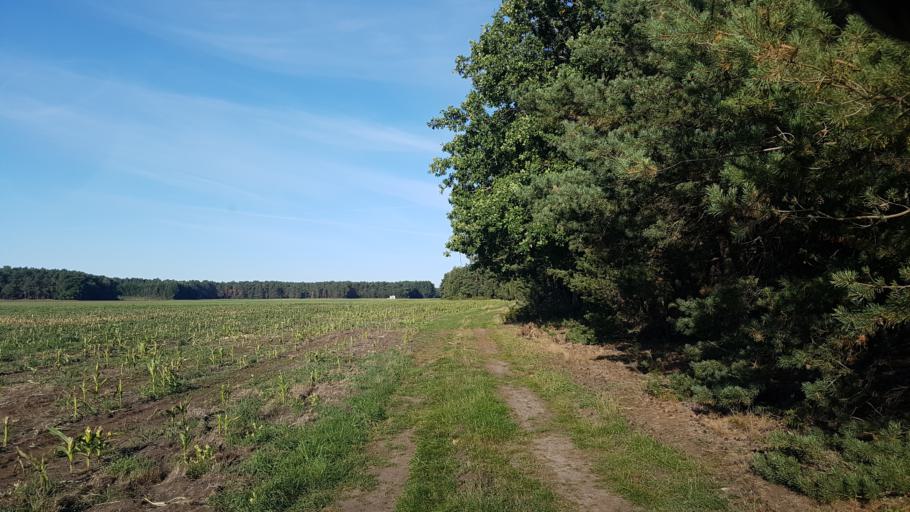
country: DE
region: Brandenburg
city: Finsterwalde
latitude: 51.5792
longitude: 13.6845
